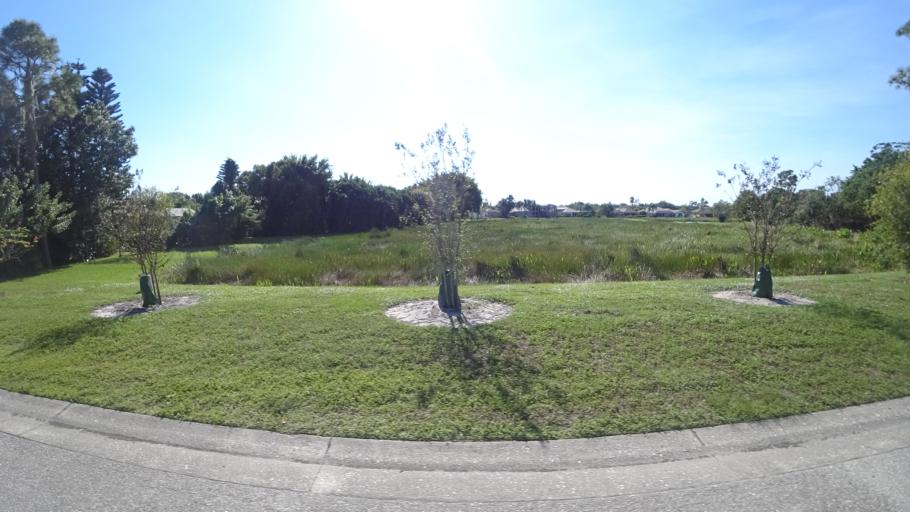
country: US
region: Florida
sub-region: Sarasota County
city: The Meadows
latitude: 27.4066
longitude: -82.4385
